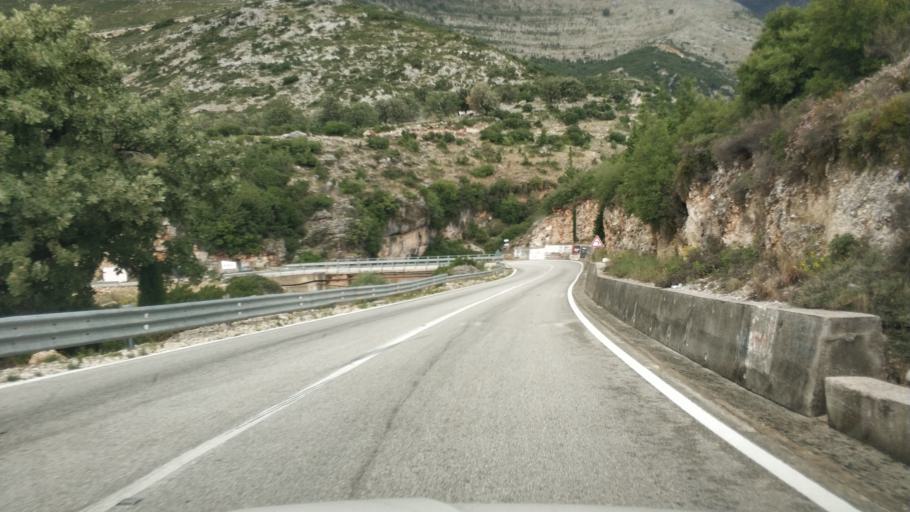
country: AL
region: Vlore
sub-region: Rrethi i Vlores
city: Vranisht
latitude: 40.1744
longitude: 19.6070
